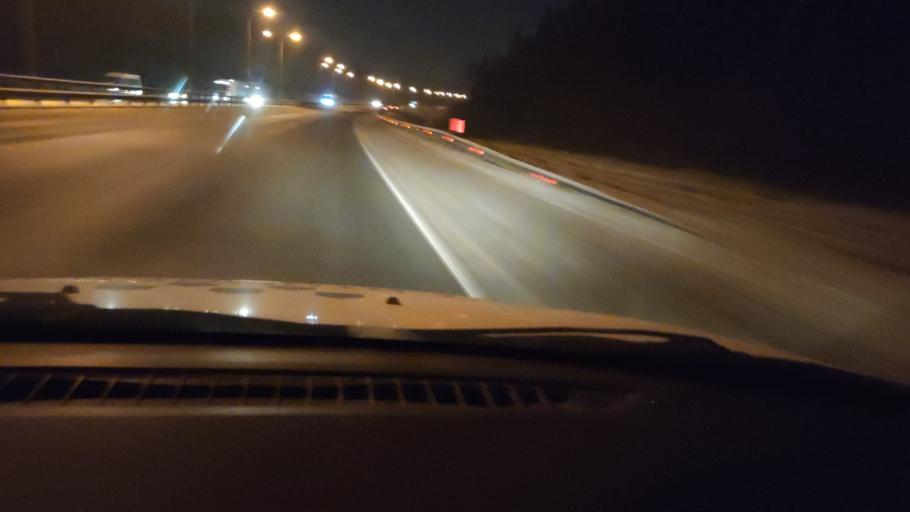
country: RU
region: Perm
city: Lobanovo
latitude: 57.8556
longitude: 56.2634
